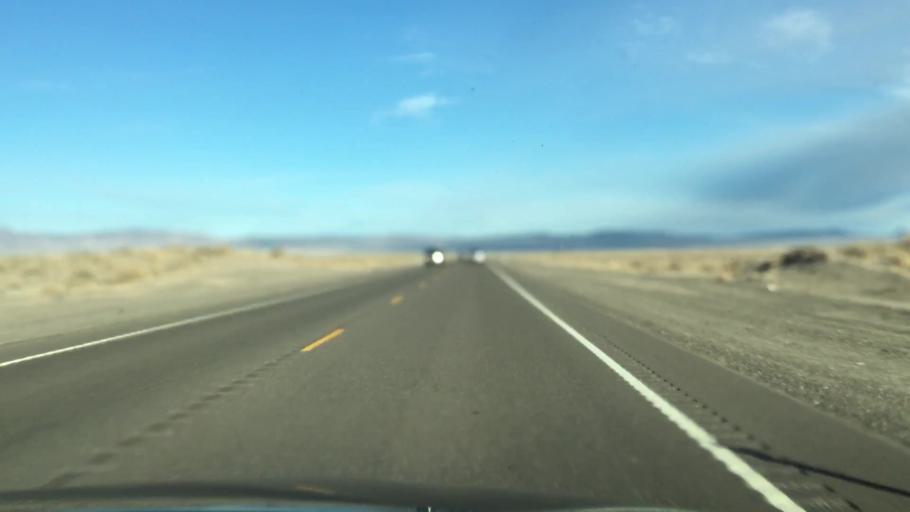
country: US
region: Nevada
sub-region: Nye County
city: Tonopah
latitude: 38.1357
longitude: -117.5117
